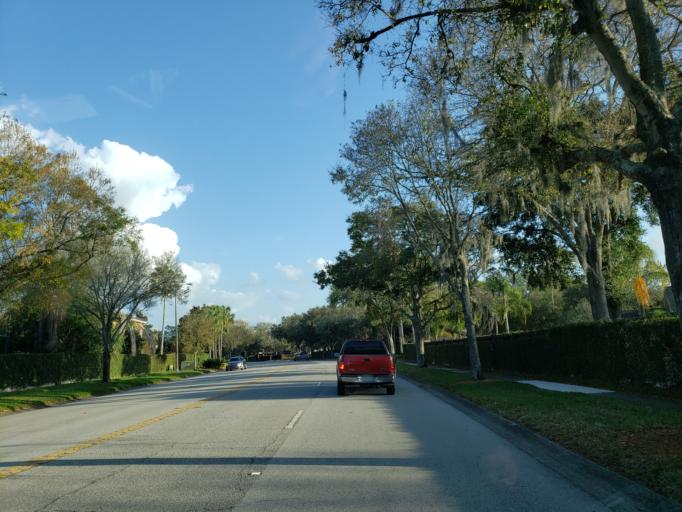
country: US
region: Florida
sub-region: Hillsborough County
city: Bloomingdale
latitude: 27.8776
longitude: -82.2657
